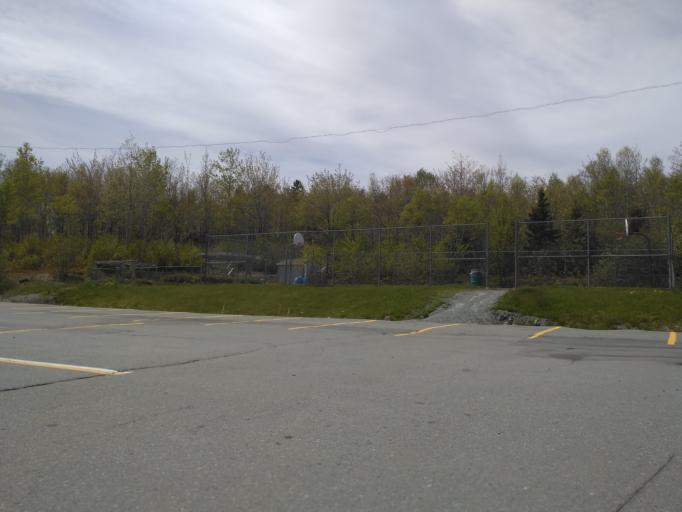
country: CA
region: Nova Scotia
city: Dartmouth
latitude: 44.7738
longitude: -63.6744
